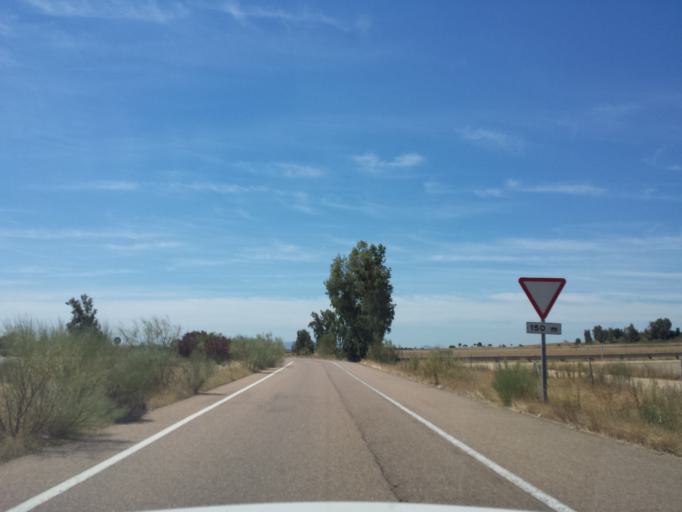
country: ES
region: Extremadura
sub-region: Provincia de Badajoz
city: Santa Amalia
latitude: 39.0040
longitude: -6.0917
